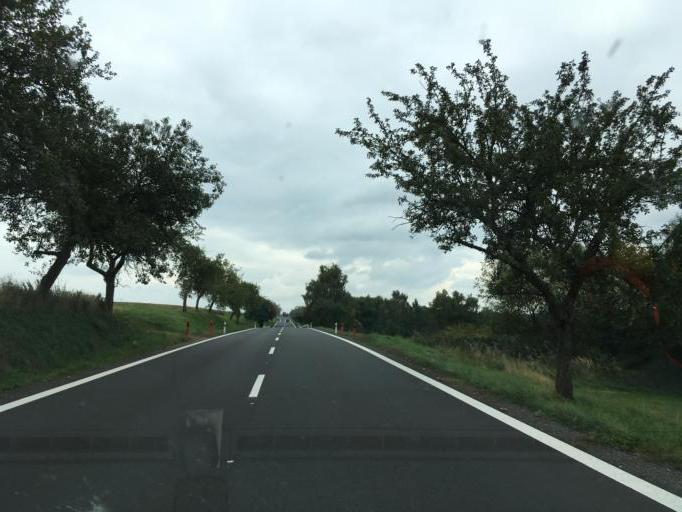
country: CZ
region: Central Bohemia
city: Cechtice
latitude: 49.5857
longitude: 15.0832
